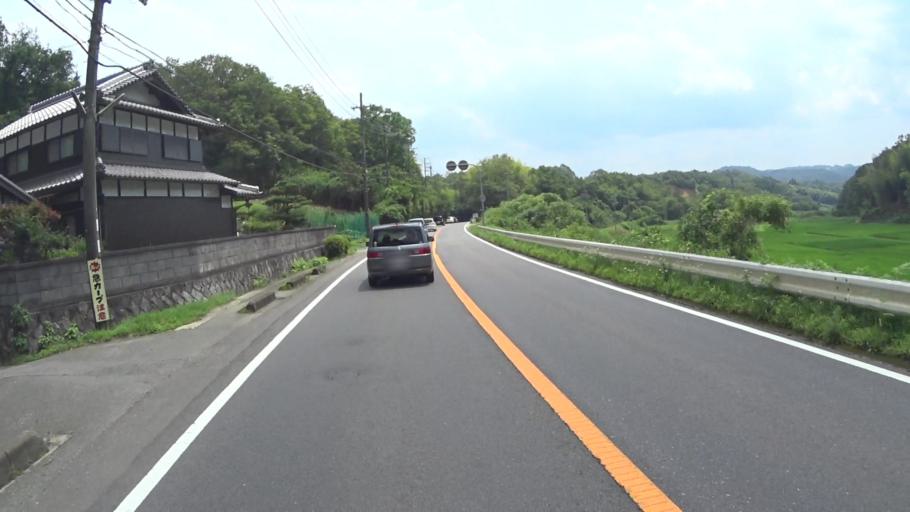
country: JP
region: Mie
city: Ueno-ebisumachi
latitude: 34.7739
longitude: 136.0187
